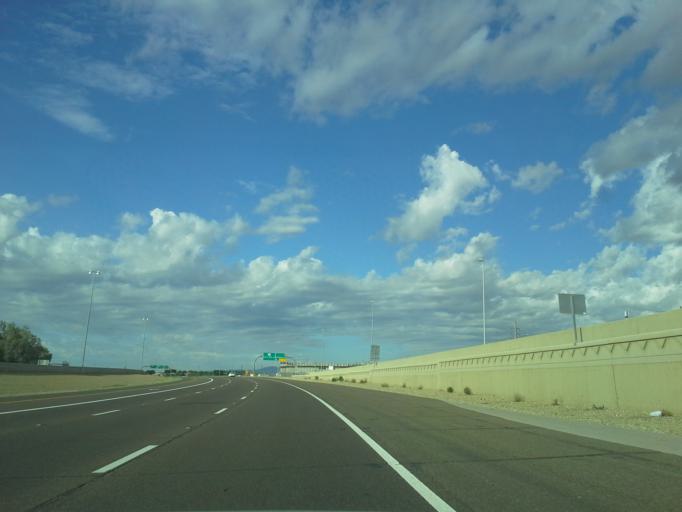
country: US
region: Arizona
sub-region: Maricopa County
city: Sun City
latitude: 33.6674
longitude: -112.2250
